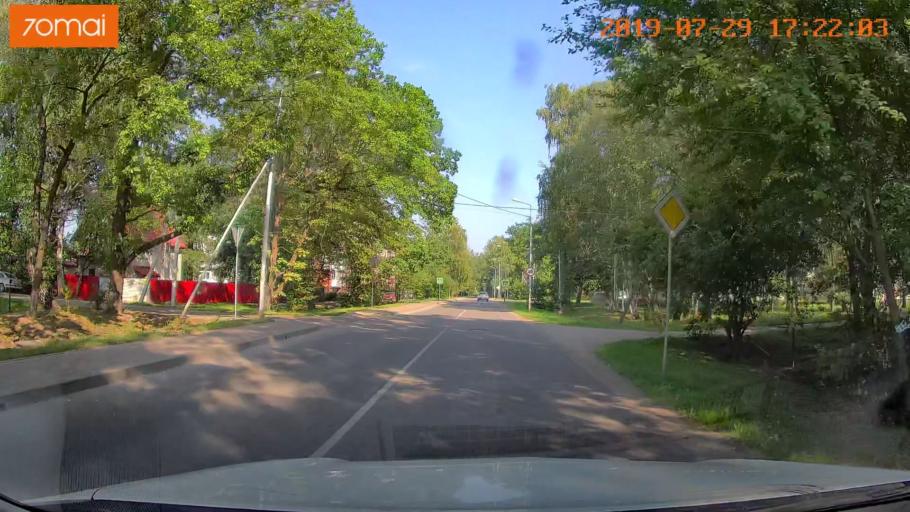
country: RU
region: Kaliningrad
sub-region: Gorod Kaliningrad
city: Kaliningrad
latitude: 54.7697
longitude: 20.4374
